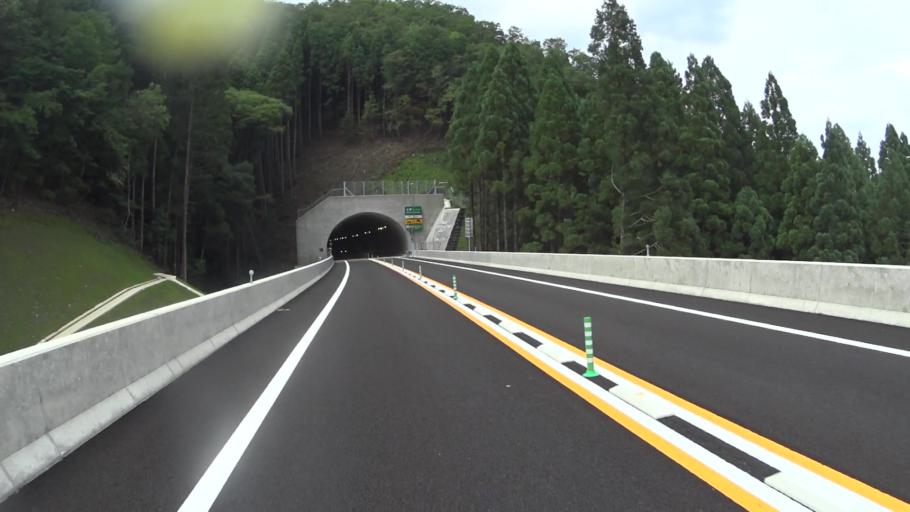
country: JP
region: Kyoto
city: Ayabe
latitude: 35.2660
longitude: 135.3453
